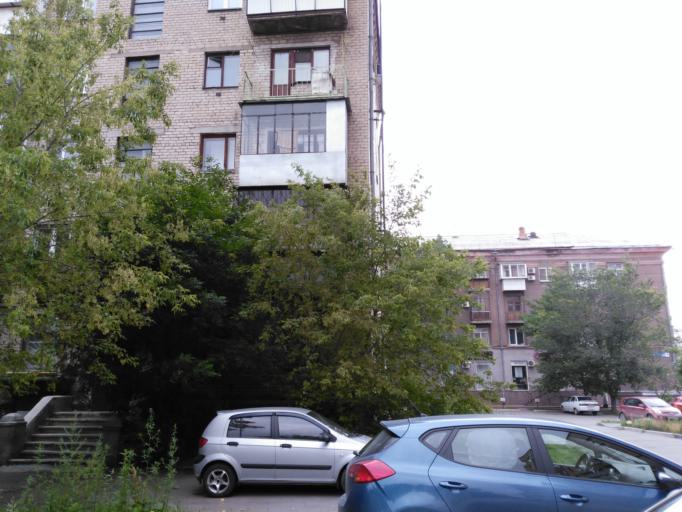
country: RU
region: Chelyabinsk
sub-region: Gorod Chelyabinsk
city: Chelyabinsk
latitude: 55.1562
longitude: 61.4111
